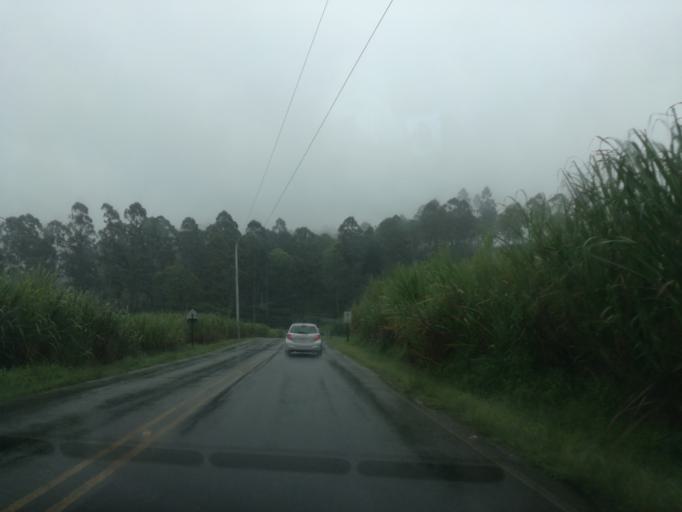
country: CR
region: Cartago
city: Tucurrique
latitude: 9.8933
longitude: -83.7648
